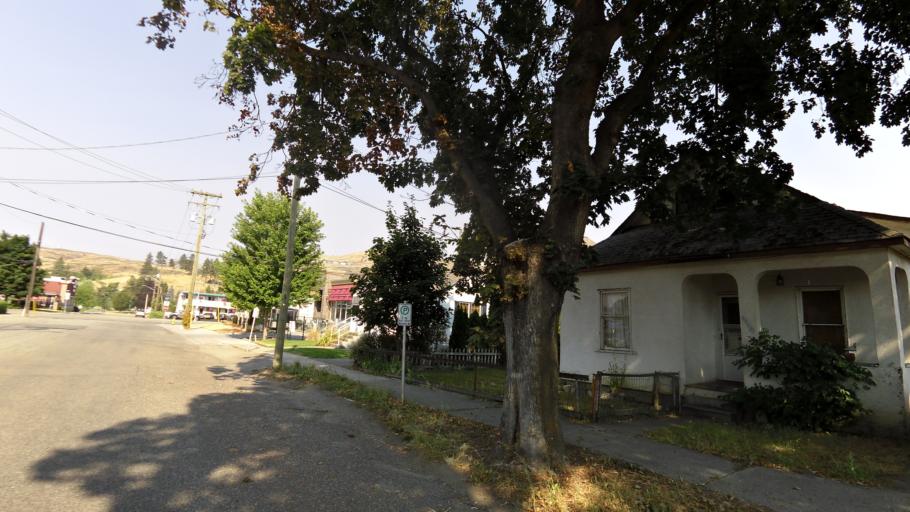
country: CA
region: British Columbia
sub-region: Regional District of North Okanagan
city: Vernon
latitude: 50.2689
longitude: -119.2725
